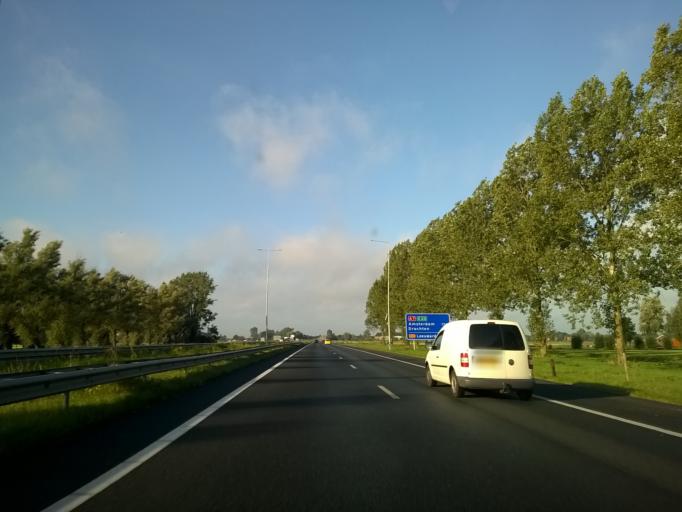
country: NL
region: Groningen
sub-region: Gemeente Zuidhorn
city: Aduard
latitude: 53.2004
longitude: 6.4635
